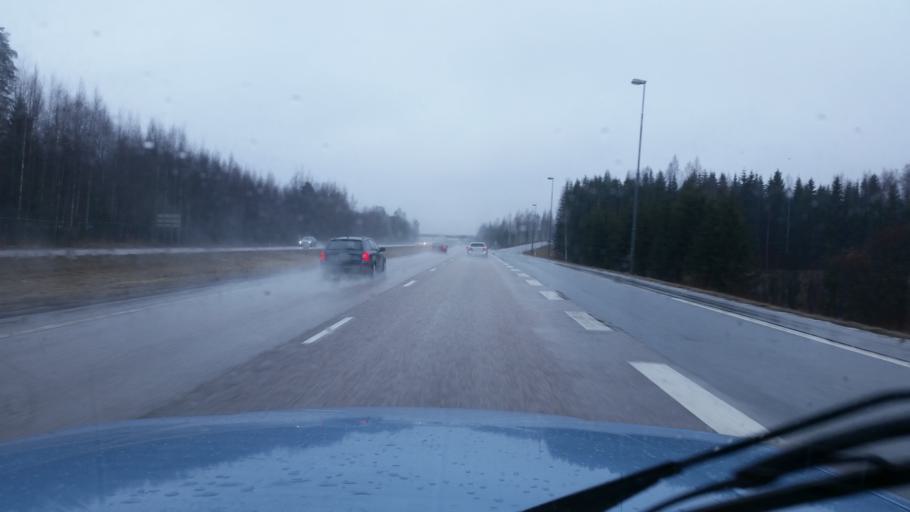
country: FI
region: Uusimaa
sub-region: Helsinki
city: Hyvinge
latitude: 60.6562
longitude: 24.7982
